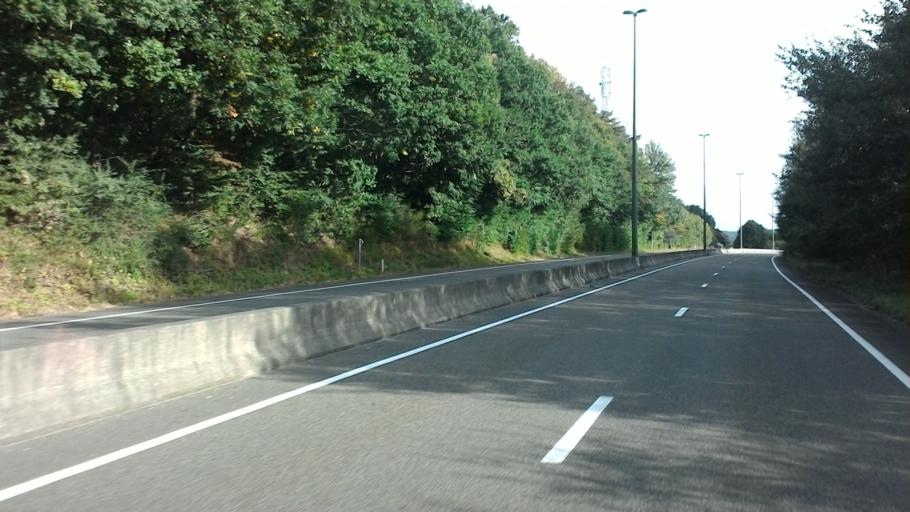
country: BE
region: Wallonia
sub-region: Province du Luxembourg
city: Attert
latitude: 49.7609
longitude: 5.7734
